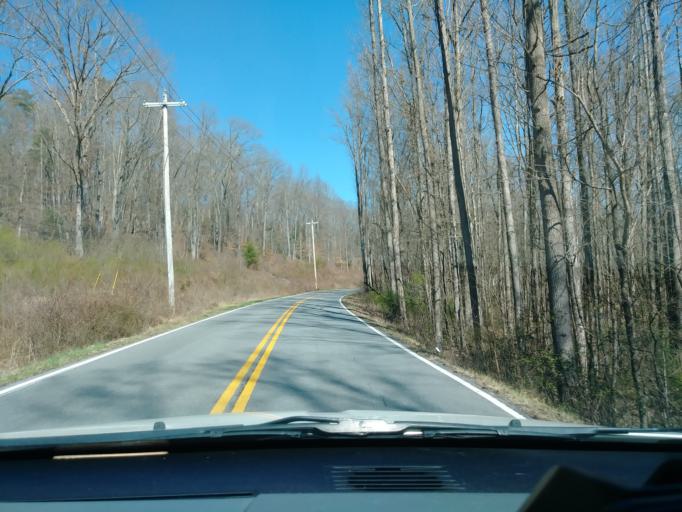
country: US
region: Tennessee
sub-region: Cocke County
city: Newport
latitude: 35.9503
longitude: -83.0536
